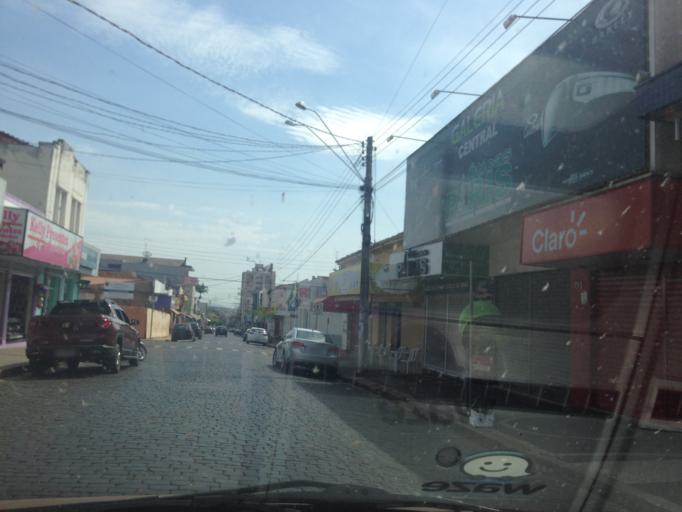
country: BR
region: Sao Paulo
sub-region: Casa Branca
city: Casa Branca
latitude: -21.7750
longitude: -47.0832
